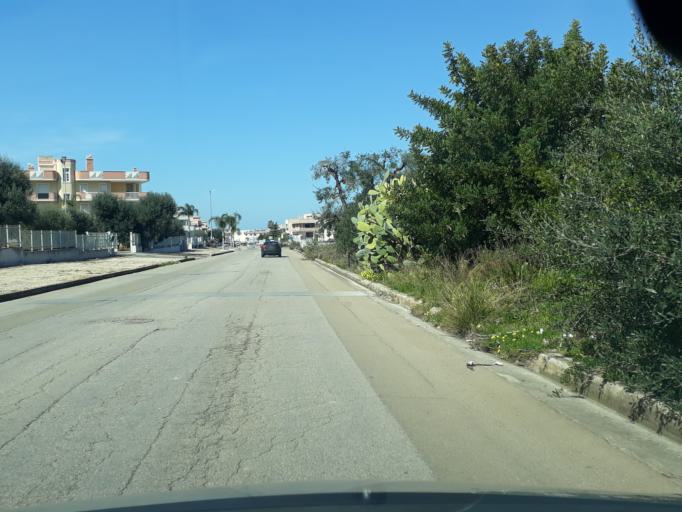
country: IT
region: Apulia
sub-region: Provincia di Brindisi
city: Fasano
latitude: 40.8469
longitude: 17.3530
